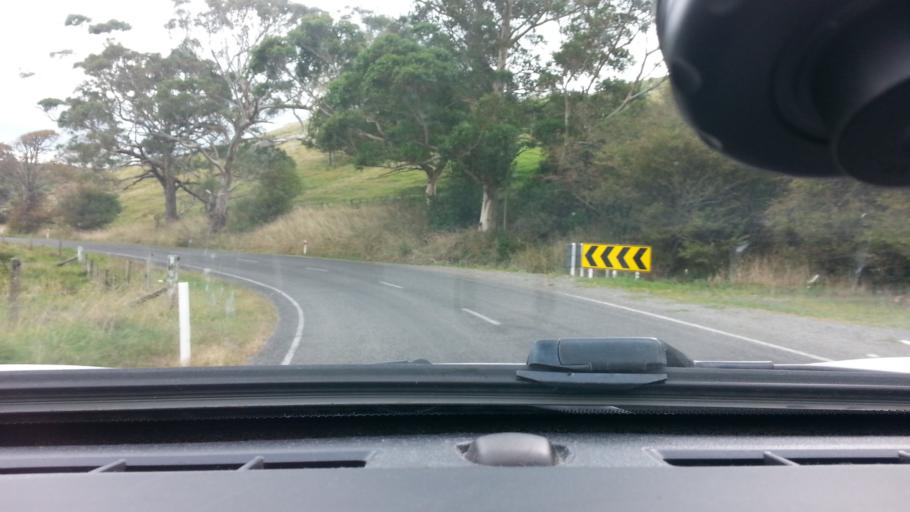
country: NZ
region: Wellington
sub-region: Upper Hutt City
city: Upper Hutt
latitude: -41.4076
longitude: 175.1961
